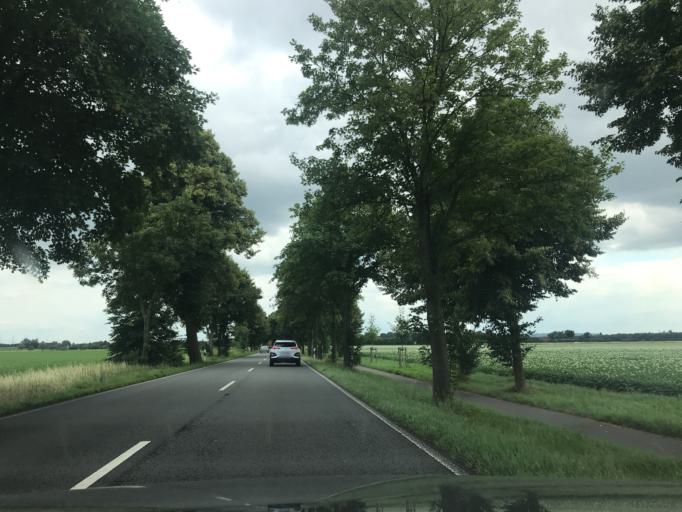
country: DE
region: North Rhine-Westphalia
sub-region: Regierungsbezirk Dusseldorf
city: Neubrueck
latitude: 51.1486
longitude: 6.6790
